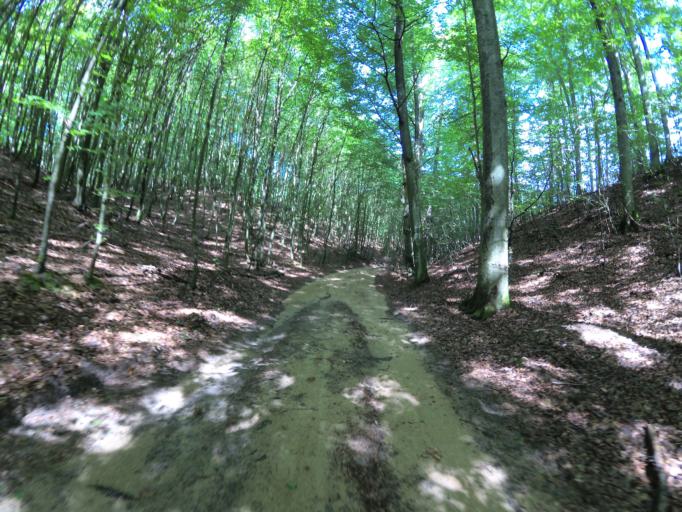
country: PL
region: Pomeranian Voivodeship
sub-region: Gdynia
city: Wielki Kack
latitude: 54.5104
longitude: 18.4503
